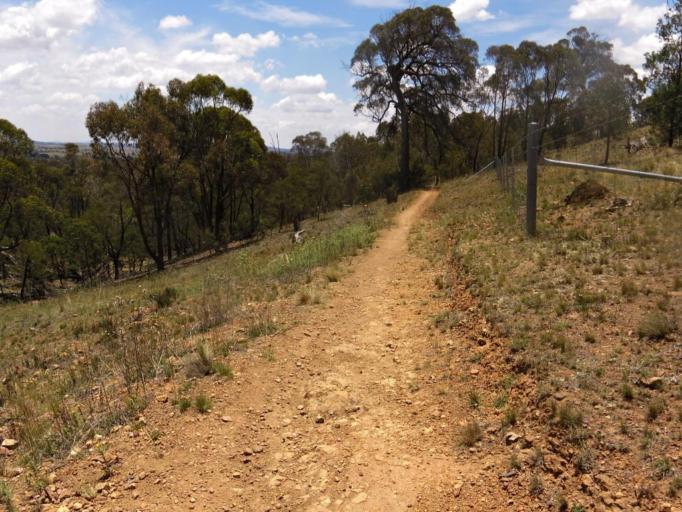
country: AU
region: Australian Capital Territory
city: Kaleen
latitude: -35.1414
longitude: 149.1472
